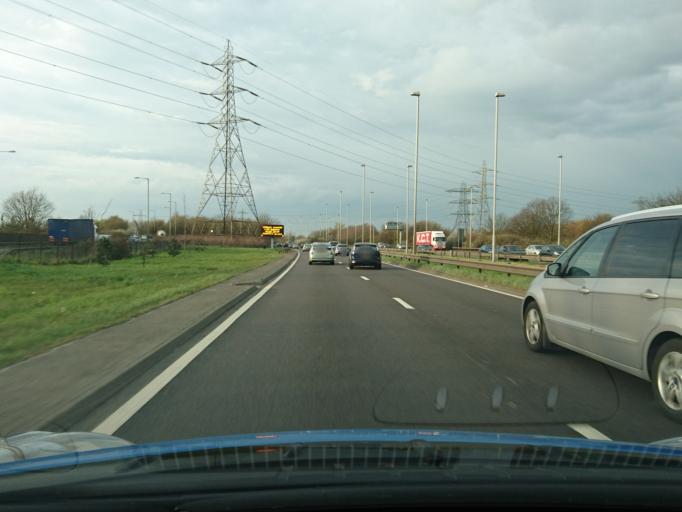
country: GB
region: England
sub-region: Greater London
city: Woodford Green
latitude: 51.5847
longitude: 0.0398
